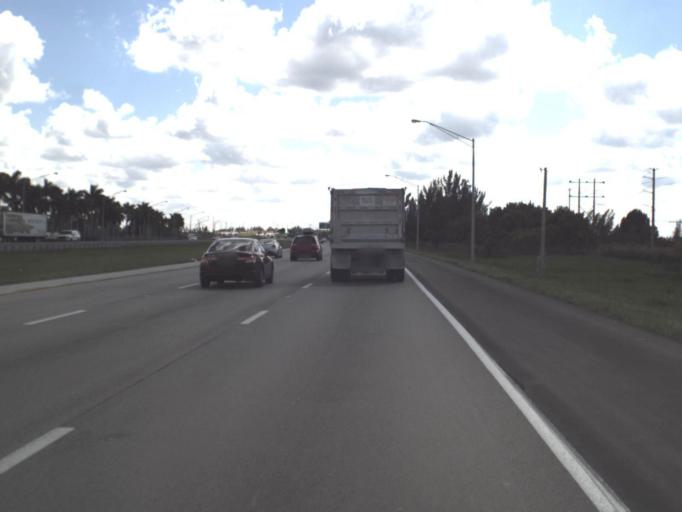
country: US
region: Florida
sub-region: Broward County
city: Tamarac
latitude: 26.2044
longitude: -80.2967
